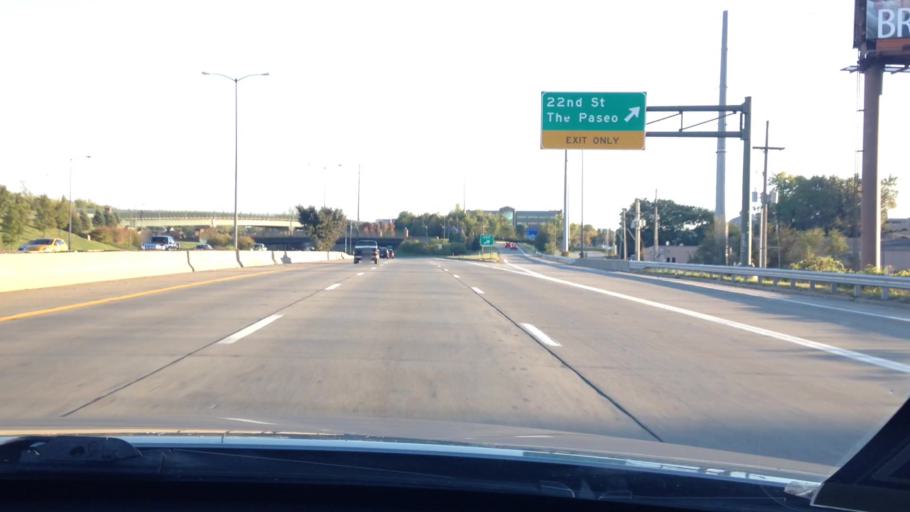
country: US
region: Missouri
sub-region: Jackson County
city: Kansas City
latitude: 39.0895
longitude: -94.5716
